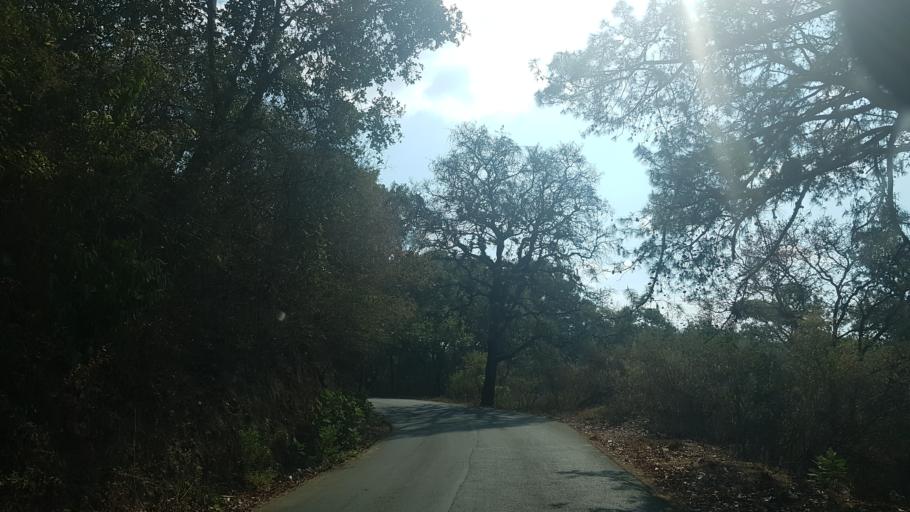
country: MX
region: Puebla
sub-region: Tochimilco
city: San Antonio Alpanocan
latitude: 18.8766
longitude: -98.7013
